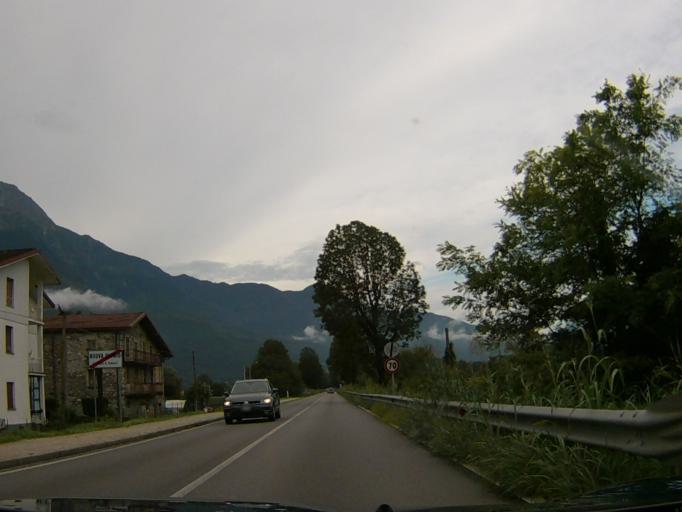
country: IT
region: Lombardy
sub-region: Provincia di Sondrio
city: Dubino
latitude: 46.1632
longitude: 9.4244
